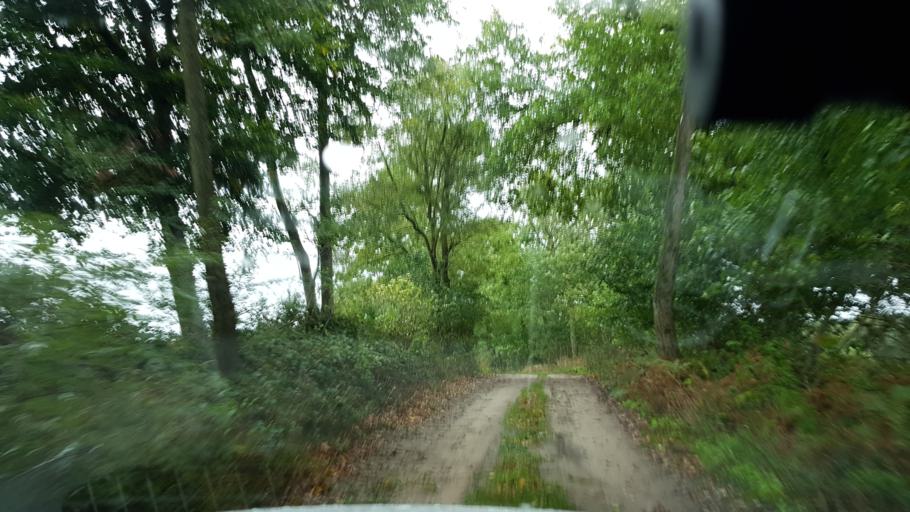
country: PL
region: West Pomeranian Voivodeship
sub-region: Powiat goleniowski
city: Przybiernow
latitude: 53.7467
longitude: 14.7594
